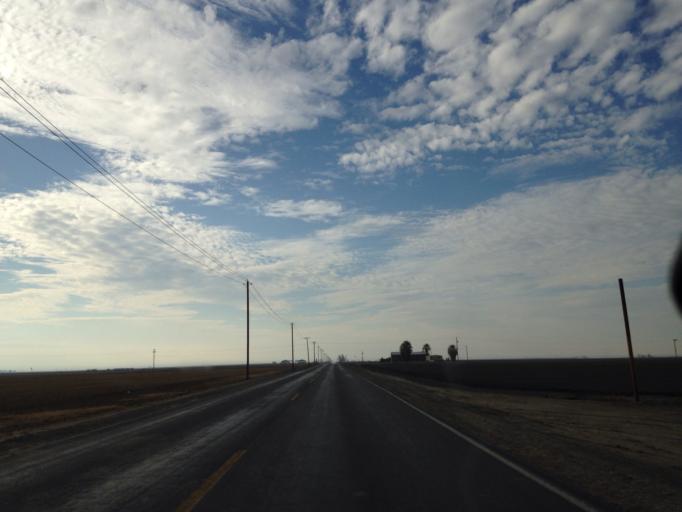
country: US
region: California
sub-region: Kern County
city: Buttonwillow
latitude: 35.4422
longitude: -119.5138
